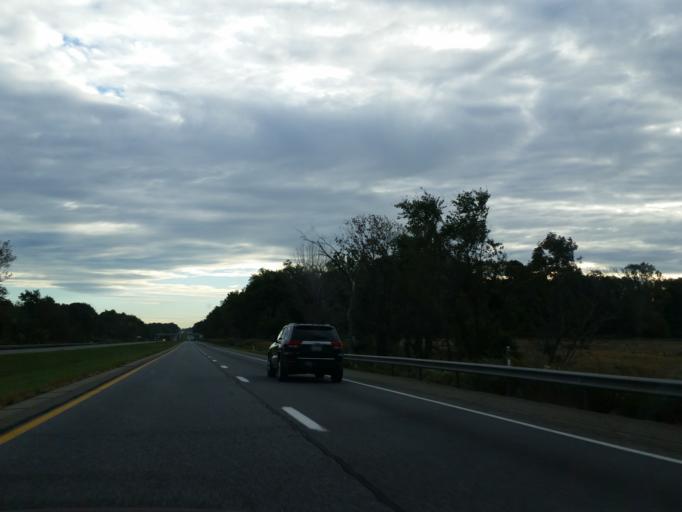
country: US
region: Pennsylvania
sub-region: Erie County
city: Albion
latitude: 41.9505
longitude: -80.3737
